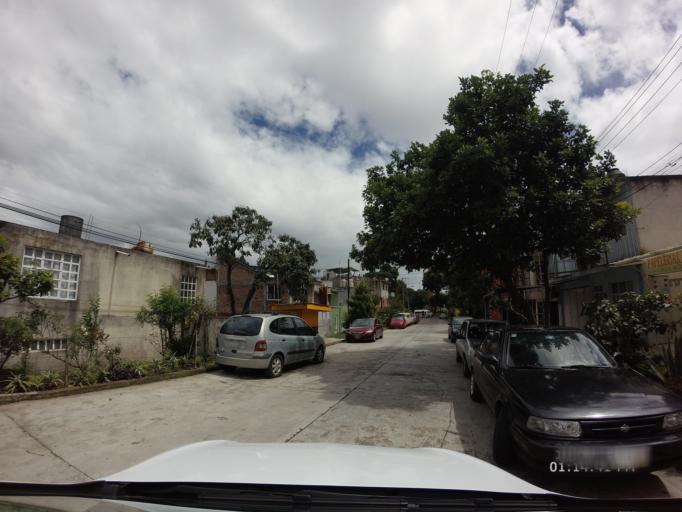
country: MX
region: Veracruz
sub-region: Tlalnelhuayocan
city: Guadalupe Victoria
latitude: 19.5597
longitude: -96.9327
